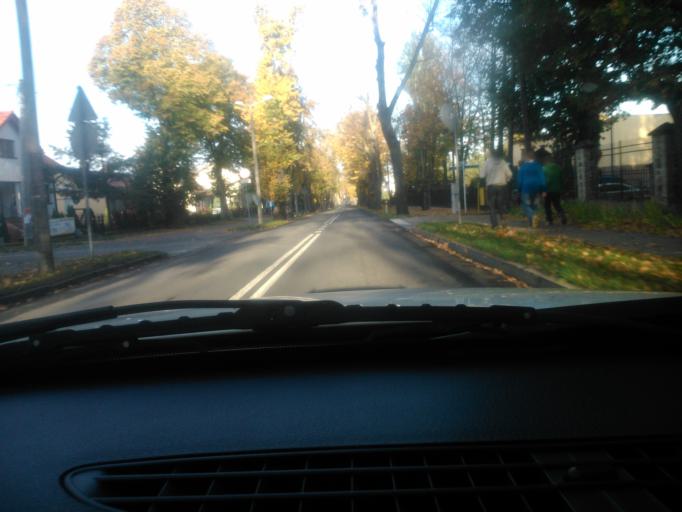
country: PL
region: Kujawsko-Pomorskie
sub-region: Powiat golubsko-dobrzynski
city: Kowalewo Pomorskie
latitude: 53.1558
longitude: 18.8919
